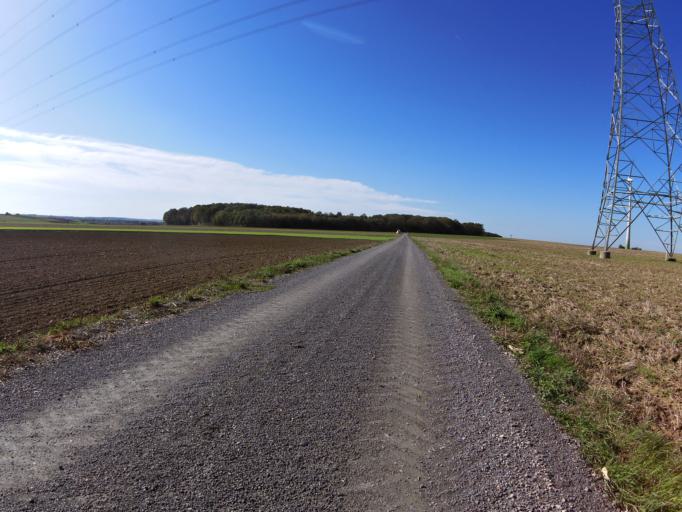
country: DE
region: Bavaria
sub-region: Regierungsbezirk Unterfranken
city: Theilheim
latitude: 49.7458
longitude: 10.0540
